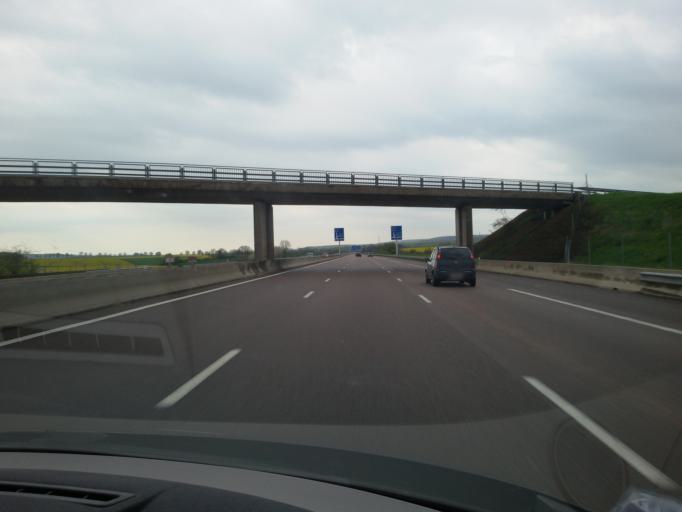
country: FR
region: Champagne-Ardenne
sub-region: Departement de la Haute-Marne
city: Rolampont
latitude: 47.8976
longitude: 5.2240
